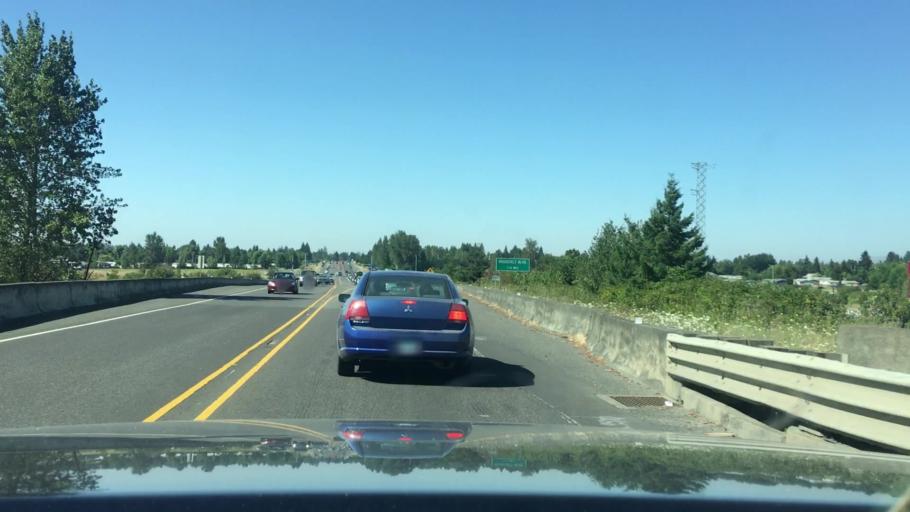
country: US
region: Oregon
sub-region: Lane County
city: Eugene
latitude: 44.0605
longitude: -123.1736
